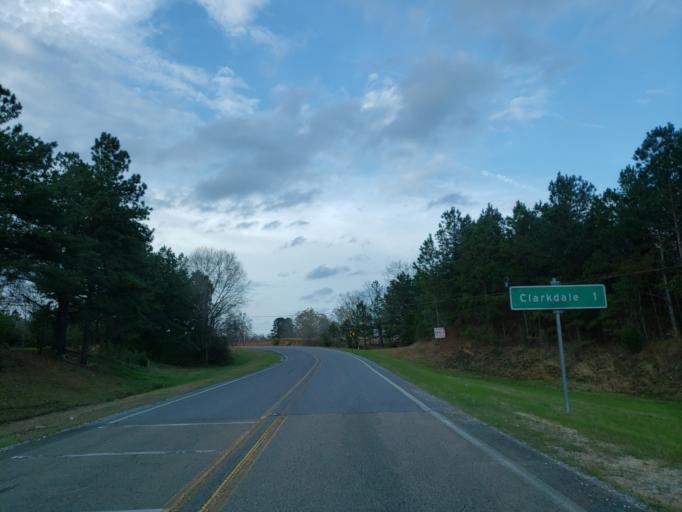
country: US
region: Mississippi
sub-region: Clarke County
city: Stonewall
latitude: 32.2152
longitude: -88.6988
